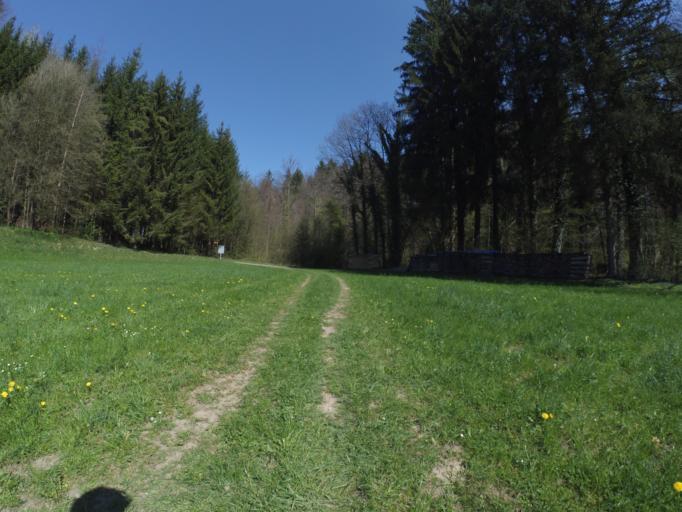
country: CH
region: Thurgau
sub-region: Frauenfeld District
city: Frauenfeld
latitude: 47.5947
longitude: 8.9117
